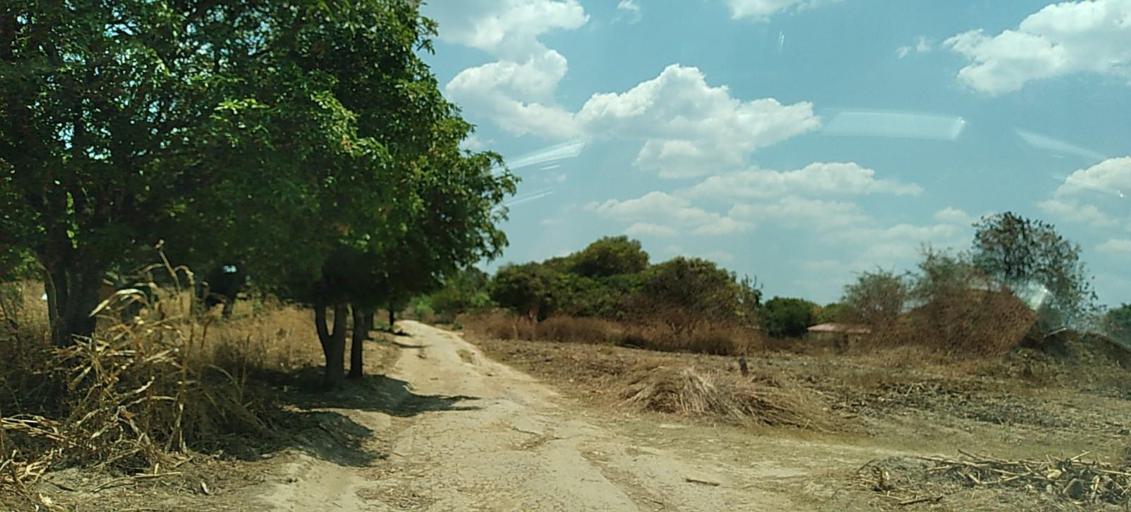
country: ZM
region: Copperbelt
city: Chililabombwe
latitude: -12.4858
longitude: 27.6685
